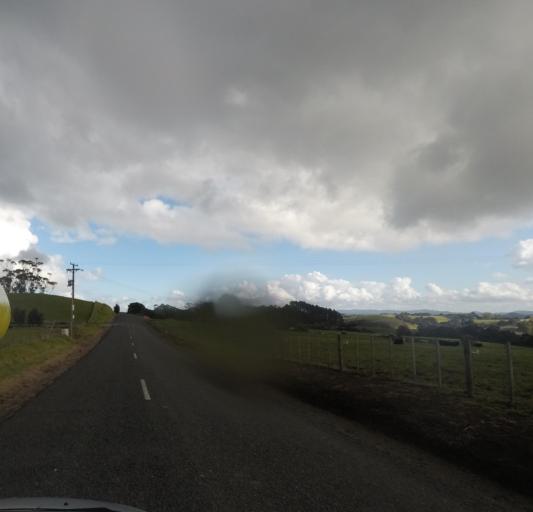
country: NZ
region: Auckland
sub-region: Auckland
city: Warkworth
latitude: -36.3701
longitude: 174.7655
